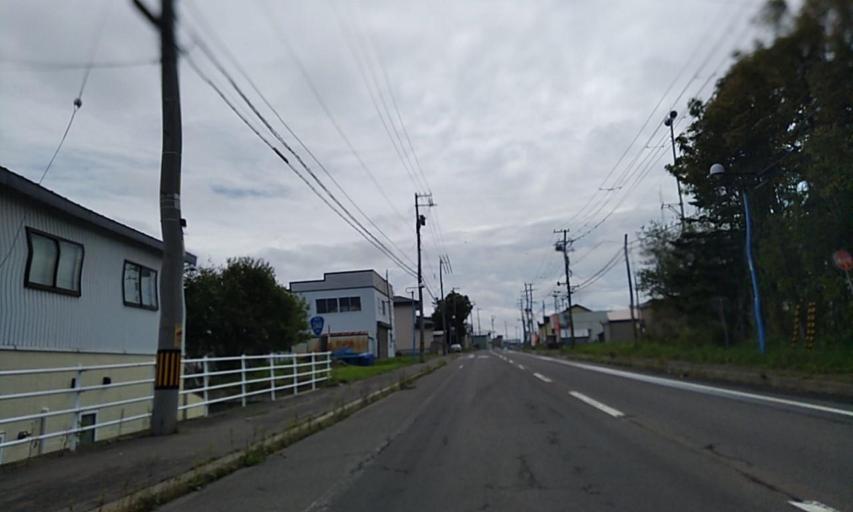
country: JP
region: Hokkaido
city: Shibetsu
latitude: 43.5745
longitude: 145.2171
